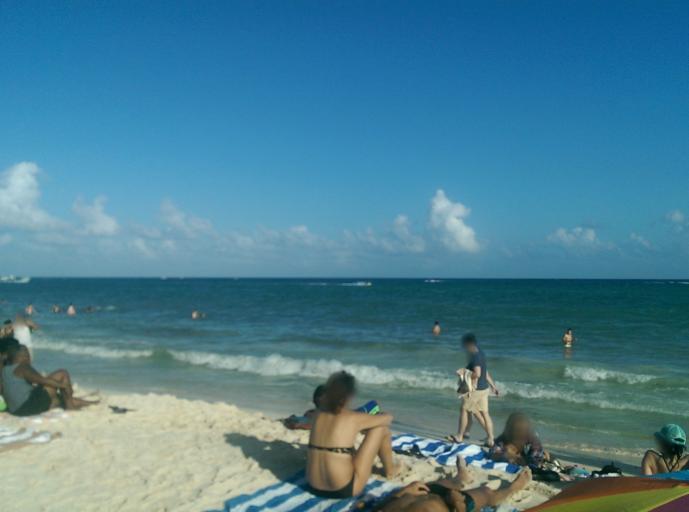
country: MX
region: Quintana Roo
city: Playa del Carmen
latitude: 20.6318
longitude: -87.0644
